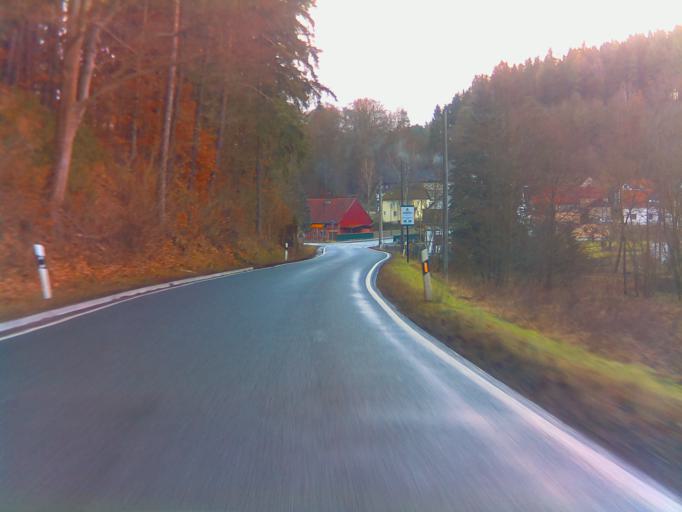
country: DE
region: Thuringia
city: Konigsee
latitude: 50.7041
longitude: 11.0998
